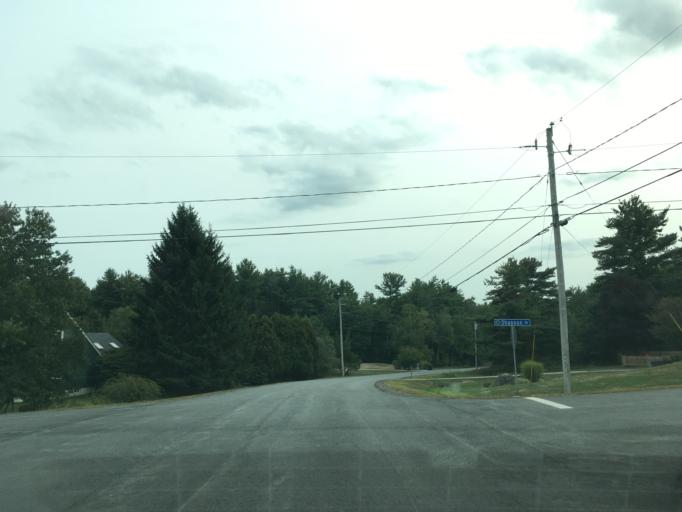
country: US
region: New Hampshire
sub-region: Rockingham County
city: Stratham Station
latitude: 43.0144
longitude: -70.8880
